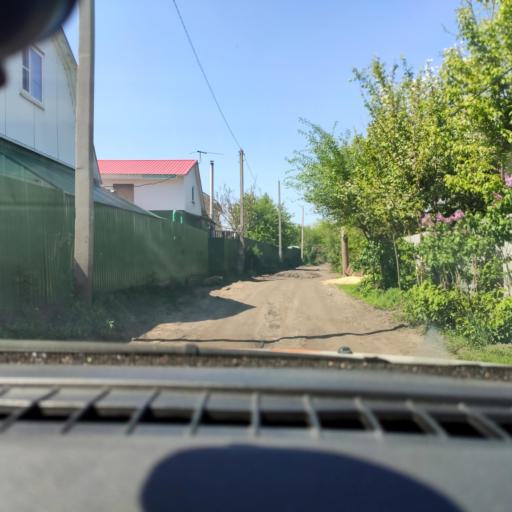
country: RU
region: Voronezj
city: Maslovka
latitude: 51.6124
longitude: 39.2762
